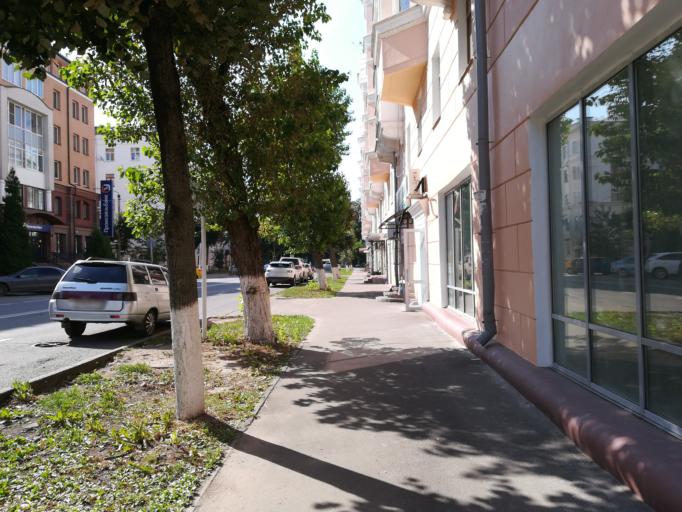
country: RU
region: Smolensk
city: Smolensk
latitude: 54.7841
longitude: 32.0438
